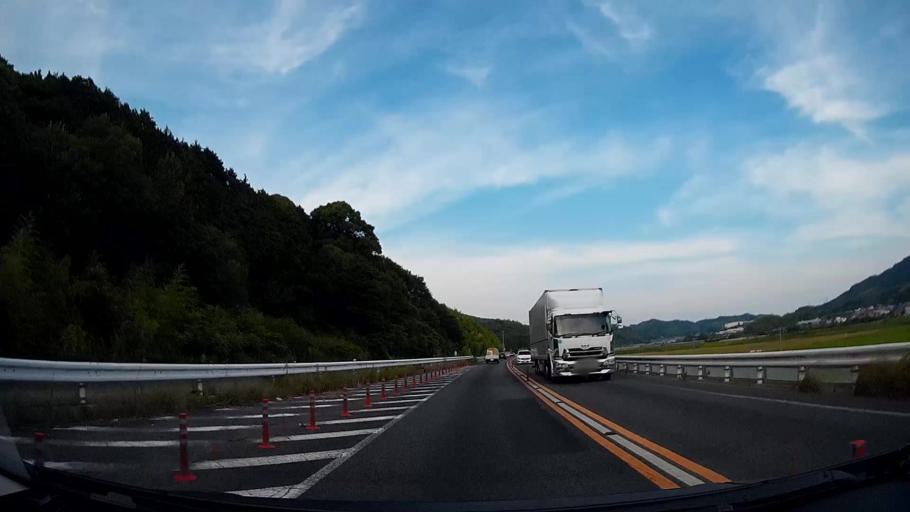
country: JP
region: Aichi
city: Nishio
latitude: 34.8615
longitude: 137.1093
